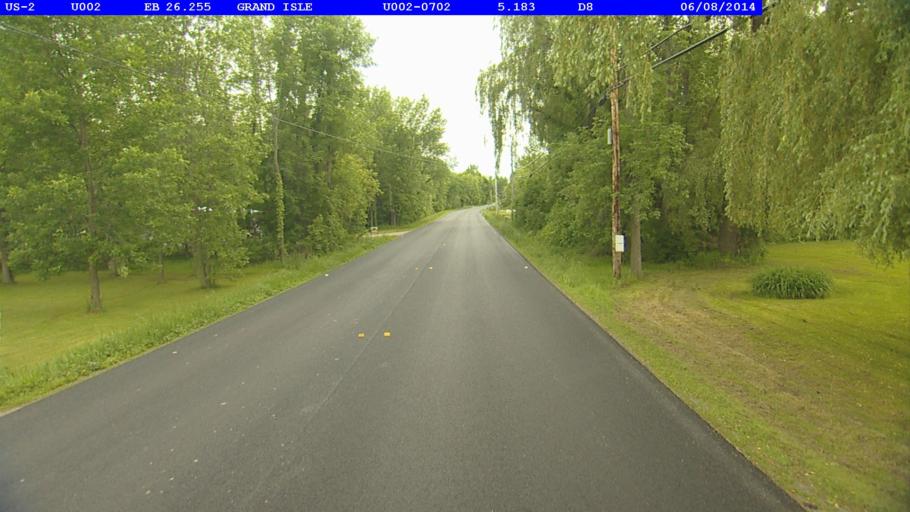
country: US
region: New York
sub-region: Clinton County
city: Cumberland Head
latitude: 44.6944
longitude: -73.3066
